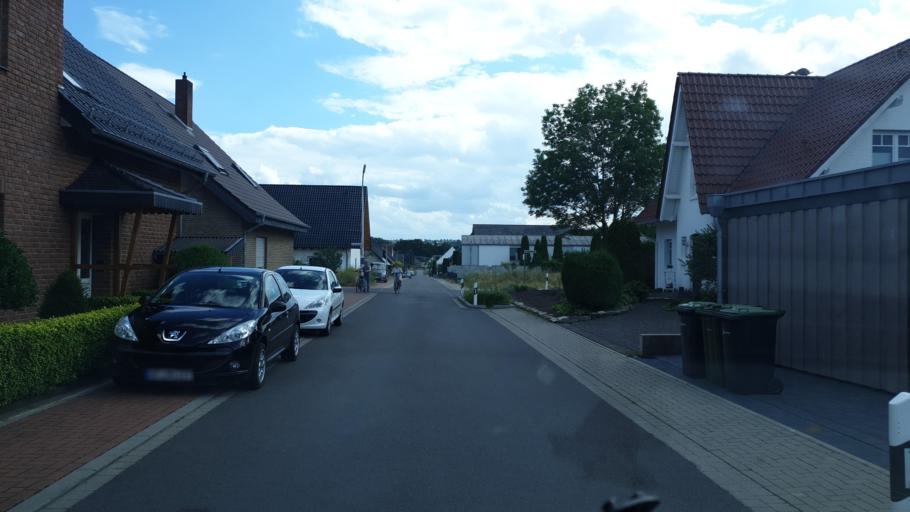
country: DE
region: North Rhine-Westphalia
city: Loehne
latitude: 52.2136
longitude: 8.7309
